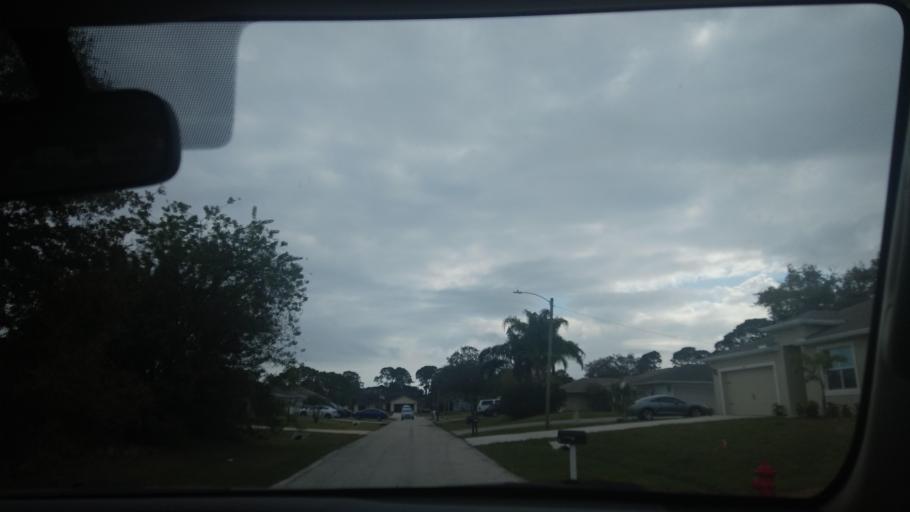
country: US
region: Florida
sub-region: Indian River County
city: Sebastian
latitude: 27.8022
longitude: -80.4903
